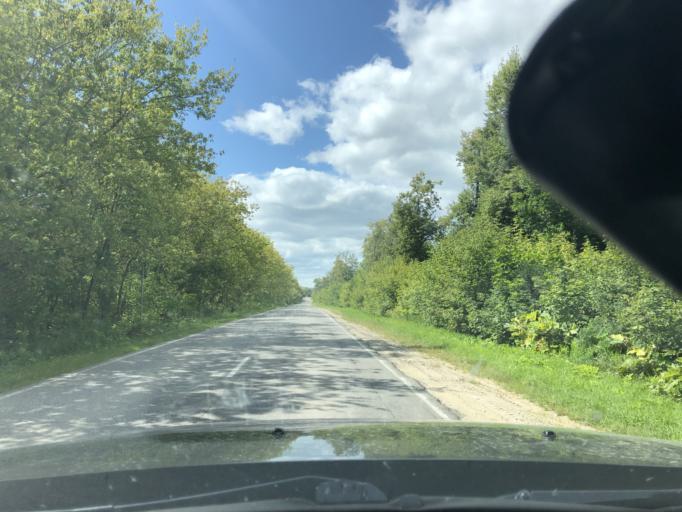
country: RU
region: Tula
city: Revyakino
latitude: 54.3437
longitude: 37.6004
